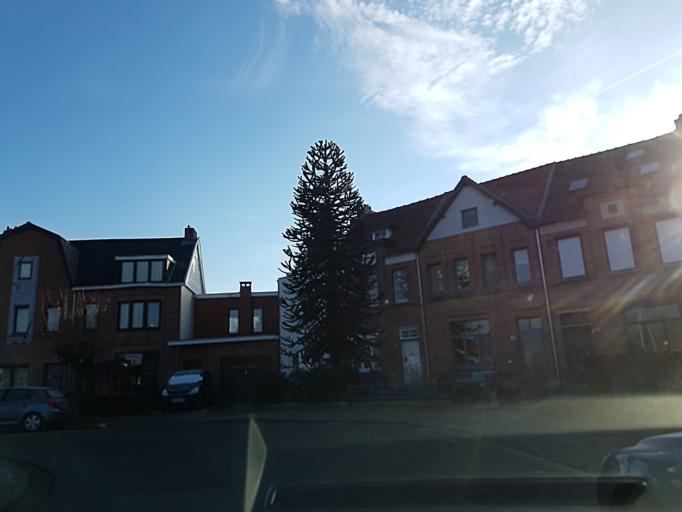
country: BE
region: Flanders
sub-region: Provincie Antwerpen
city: Aartselaar
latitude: 51.1675
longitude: 4.3834
